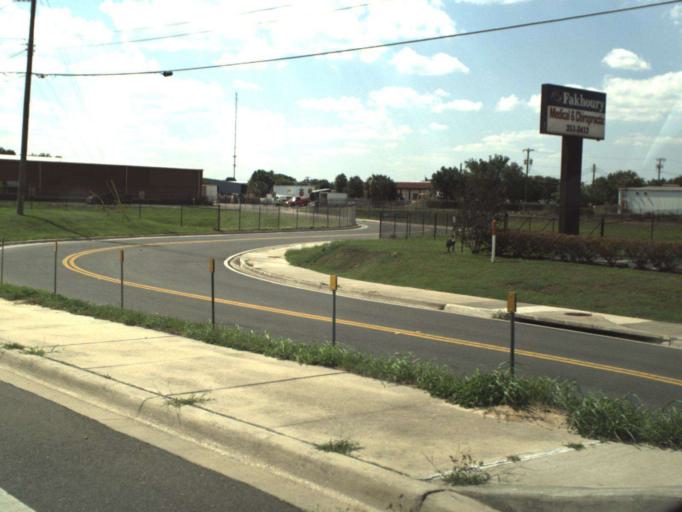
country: US
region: Florida
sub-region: Marion County
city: Ocala
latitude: 29.1717
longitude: -82.1473
